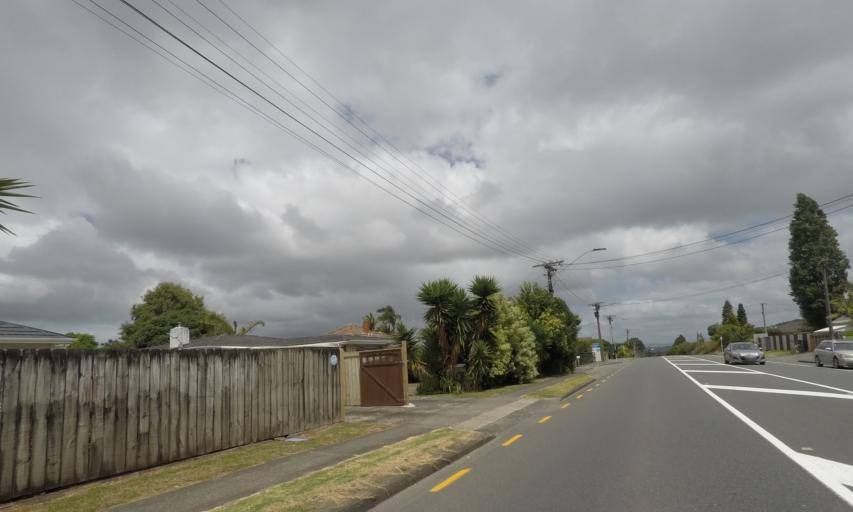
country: NZ
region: Northland
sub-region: Whangarei
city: Whangarei
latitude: -35.6947
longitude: 174.3115
